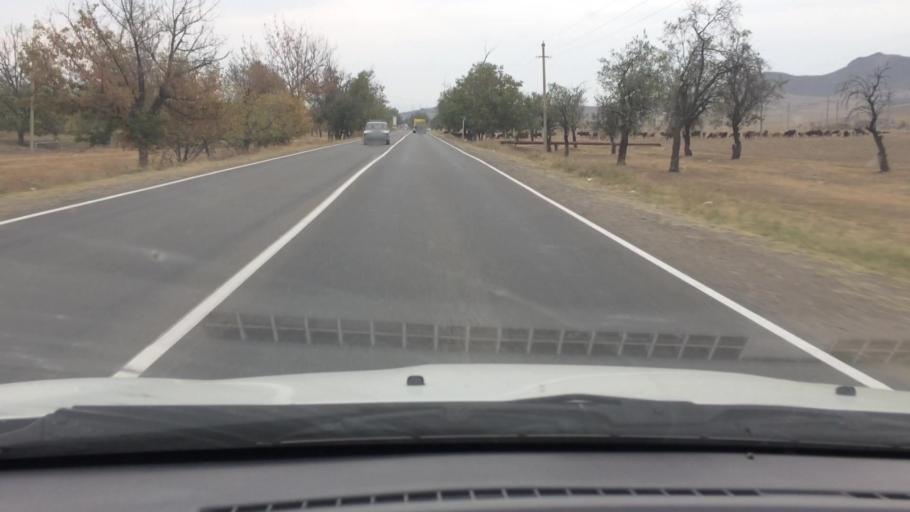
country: GE
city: Naghvarevi
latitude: 41.3851
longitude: 44.8297
